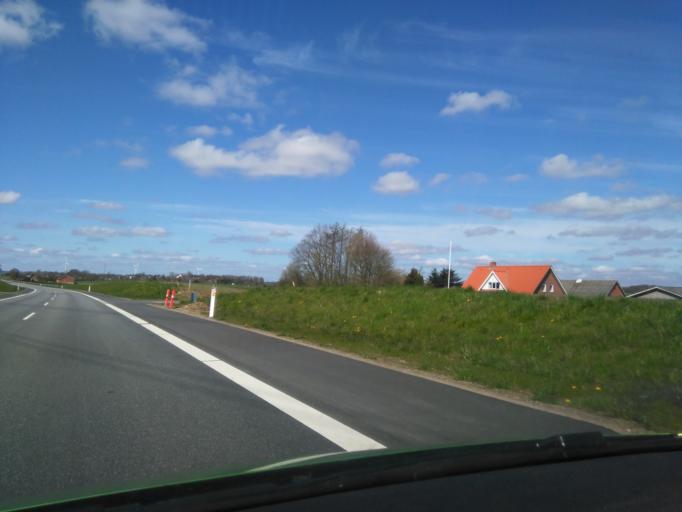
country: DK
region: Central Jutland
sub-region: Arhus Kommune
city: Solbjerg
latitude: 55.9789
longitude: 10.0732
